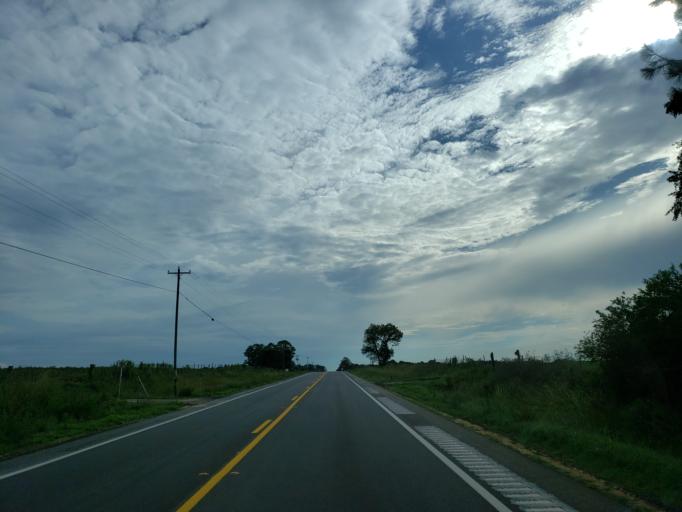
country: US
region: Georgia
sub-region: Irwin County
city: Ocilla
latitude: 31.5911
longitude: -83.2669
